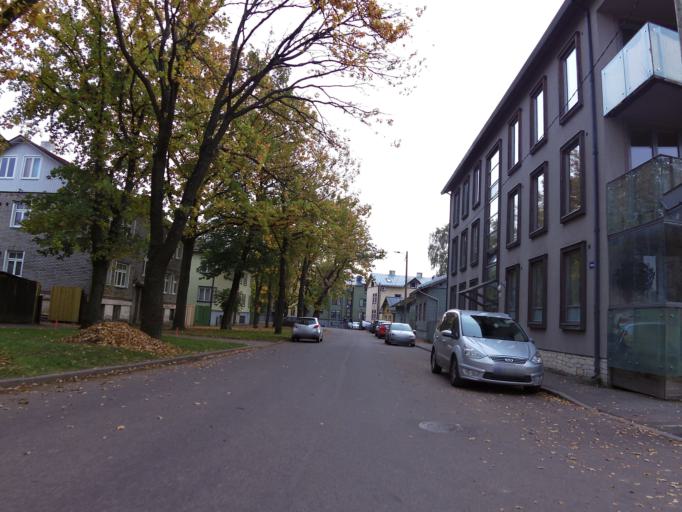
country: EE
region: Harju
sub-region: Tallinna linn
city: Tallinn
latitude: 59.4407
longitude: 24.7193
